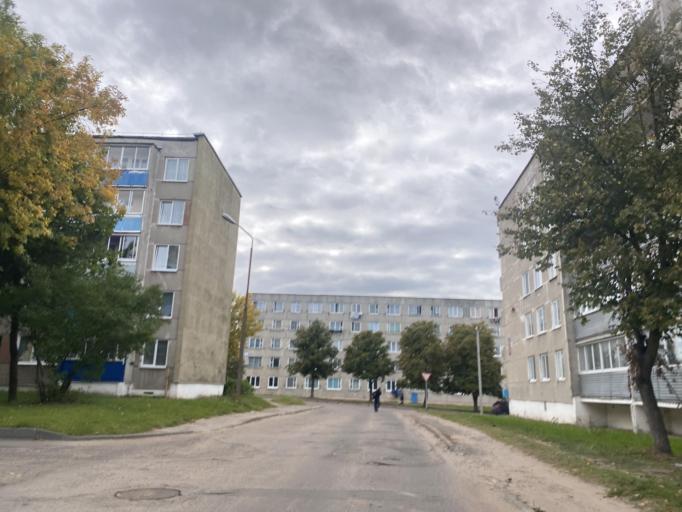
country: BY
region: Grodnenskaya
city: Smarhon'
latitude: 54.4830
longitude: 26.3984
